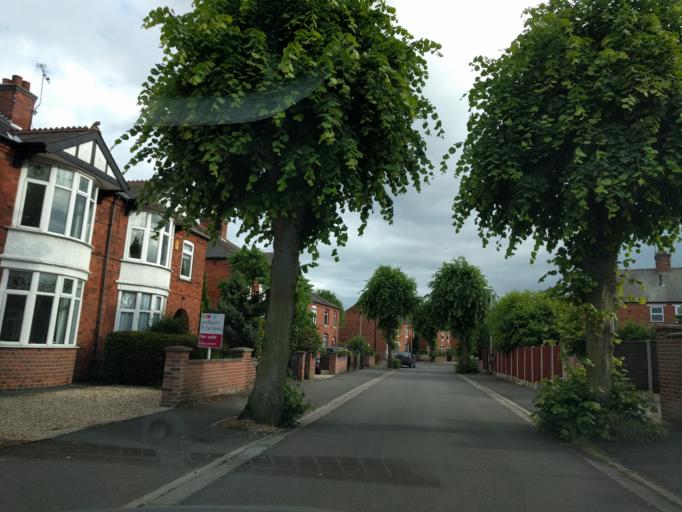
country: GB
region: England
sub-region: Nottinghamshire
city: Newark on Trent
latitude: 53.0713
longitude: -0.8114
